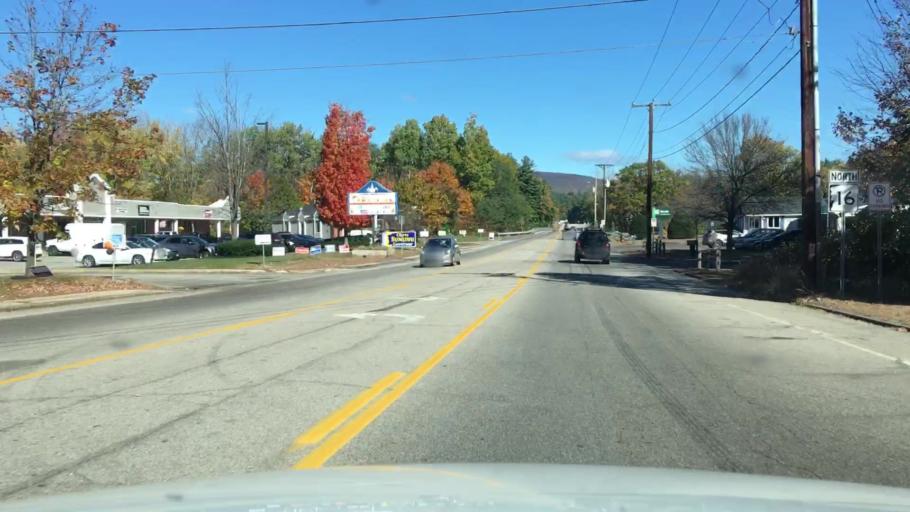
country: US
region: New Hampshire
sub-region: Carroll County
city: Conway
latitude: 43.9795
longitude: -71.1165
